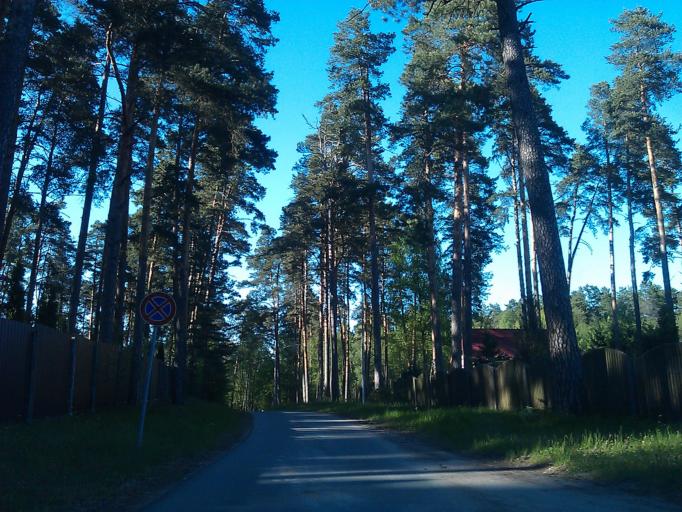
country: LV
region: Riga
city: Bergi
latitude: 57.0148
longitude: 24.2862
